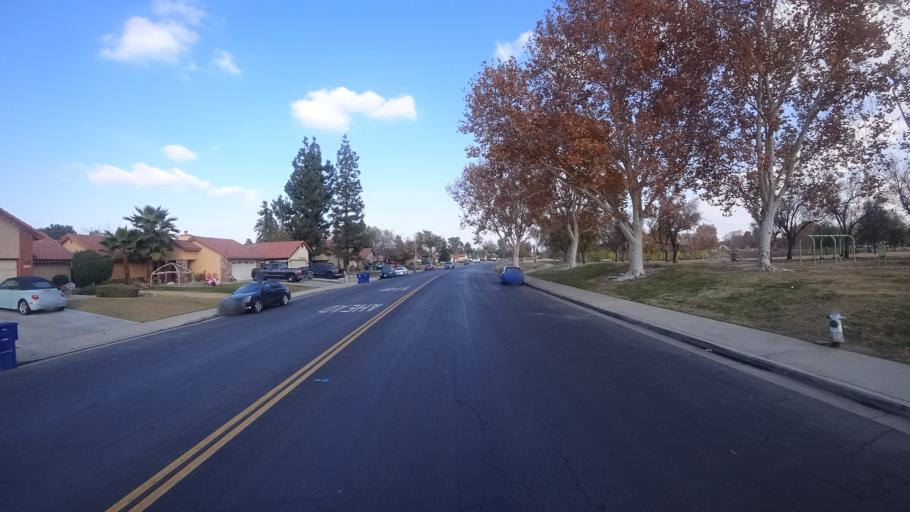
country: US
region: California
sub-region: Kern County
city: Greenacres
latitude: 35.3149
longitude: -119.1022
